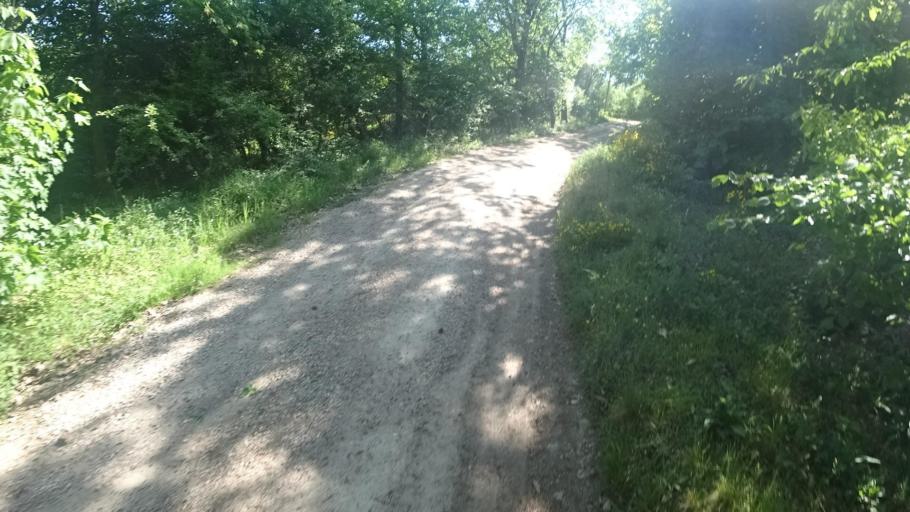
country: DE
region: Rheinland-Pfalz
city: Altenahr
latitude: 50.5223
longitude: 6.9836
